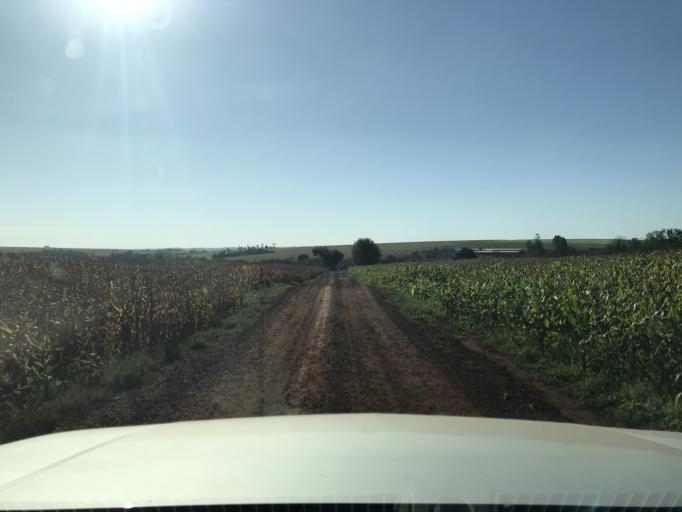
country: BR
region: Parana
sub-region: Palotina
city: Palotina
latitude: -24.2418
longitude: -53.7995
